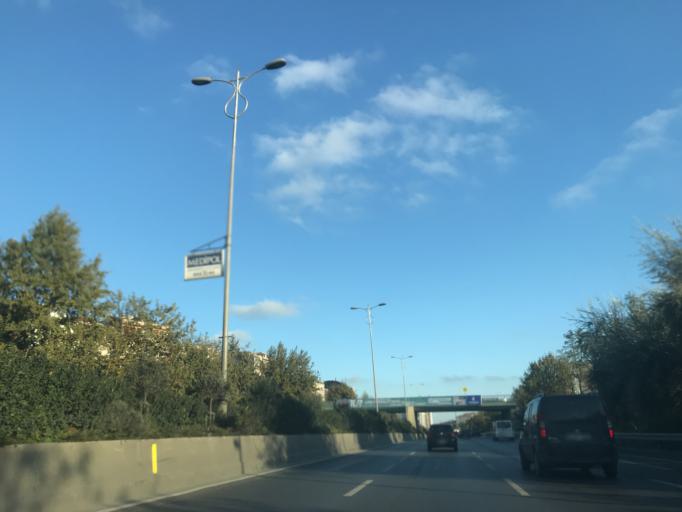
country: TR
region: Istanbul
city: Esenler
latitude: 41.0504
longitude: 28.8726
